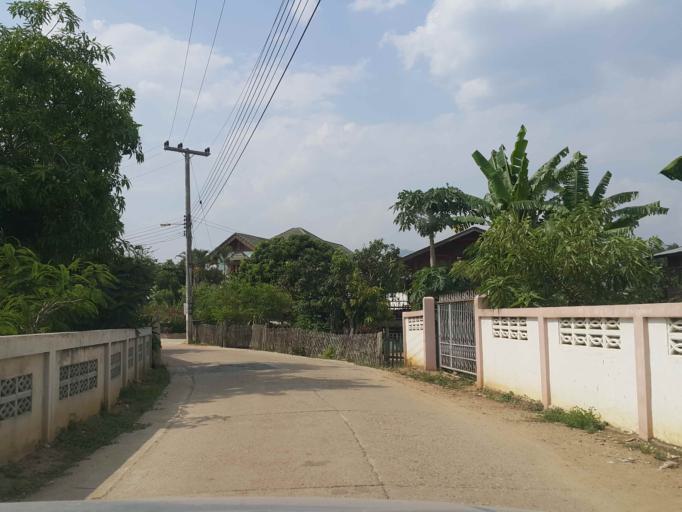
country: TH
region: Chiang Mai
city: Wiang Haeng
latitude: 19.3855
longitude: 98.7166
